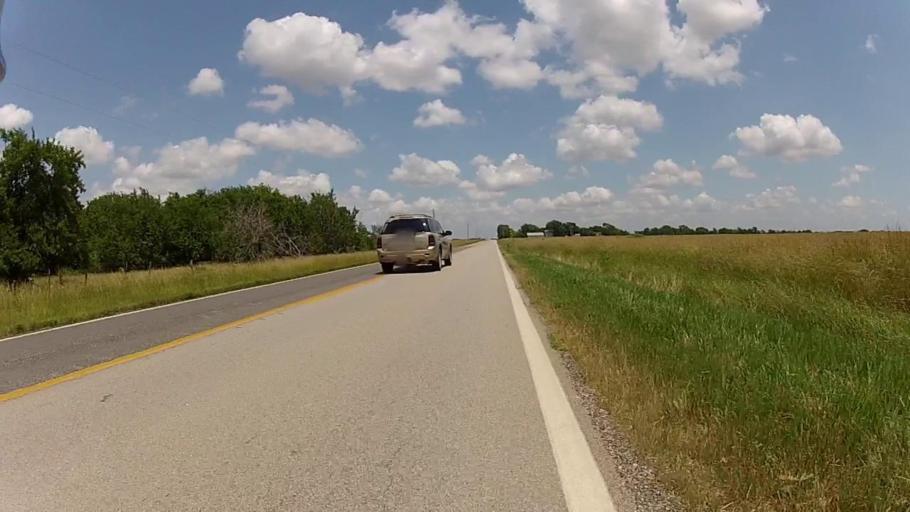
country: US
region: Kansas
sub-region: Labette County
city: Altamont
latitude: 37.1925
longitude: -95.3492
